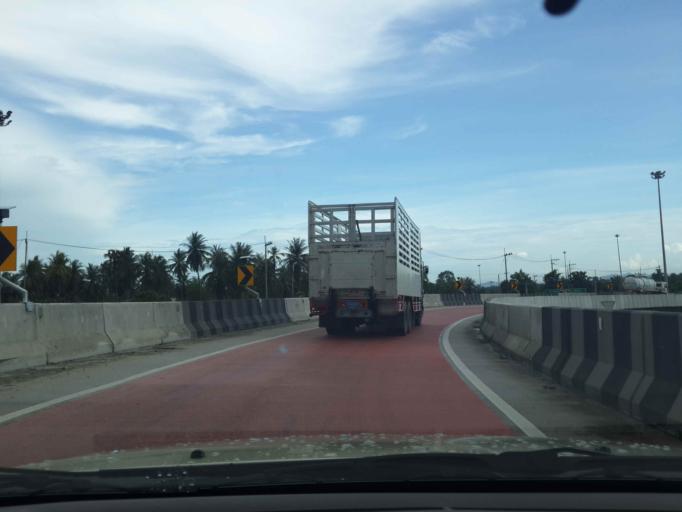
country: TH
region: Chon Buri
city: Bang Lamung
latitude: 12.9634
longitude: 100.9794
